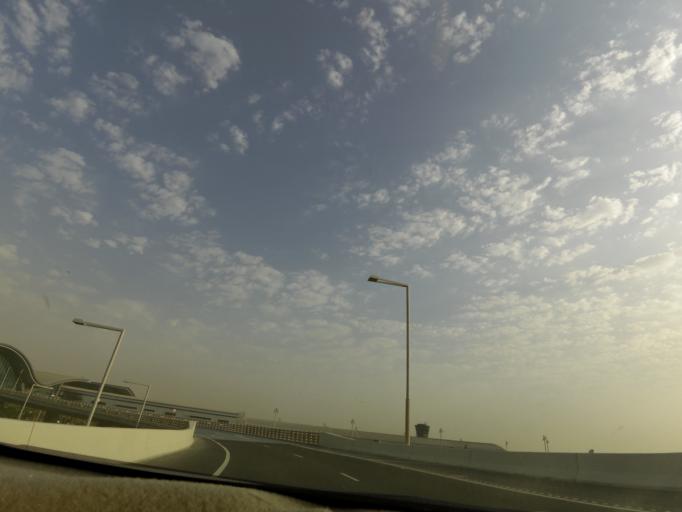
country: QA
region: Al Wakrah
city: Al Wakrah
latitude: 25.2550
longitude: 51.6169
